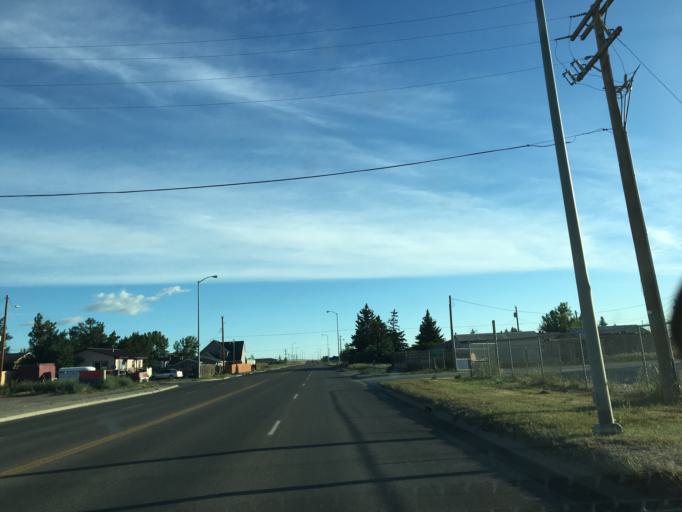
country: US
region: Montana
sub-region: Glacier County
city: Browning
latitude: 48.5582
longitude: -113.0098
